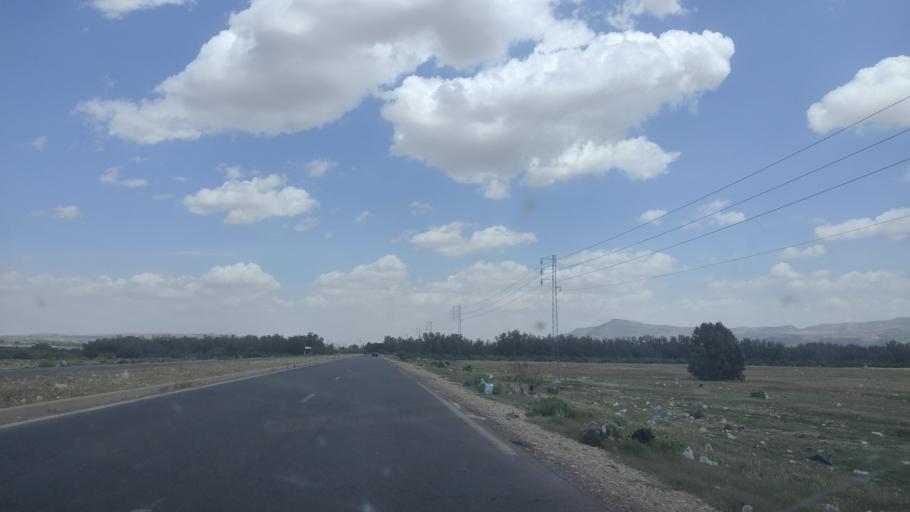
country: TN
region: Al Qasrayn
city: Kasserine
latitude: 35.1988
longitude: 8.8640
